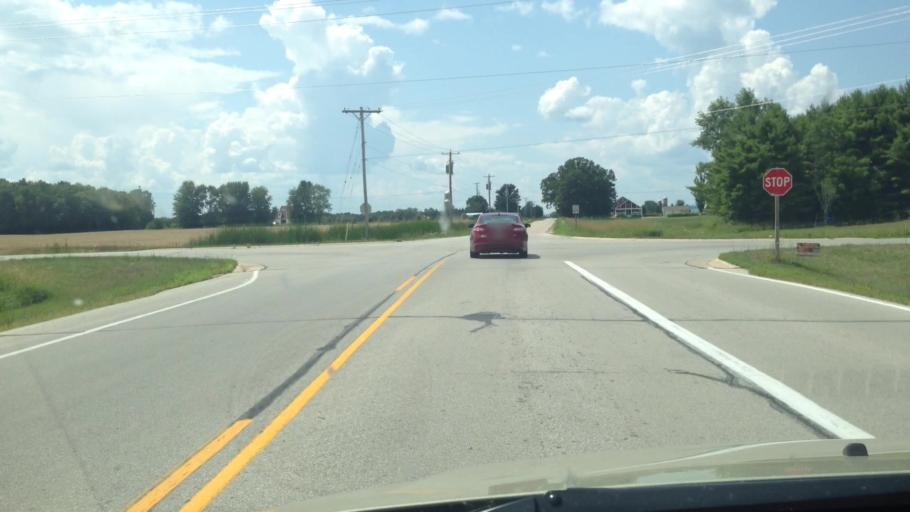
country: US
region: Wisconsin
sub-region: Brown County
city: Pulaski
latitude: 44.6565
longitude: -88.2425
